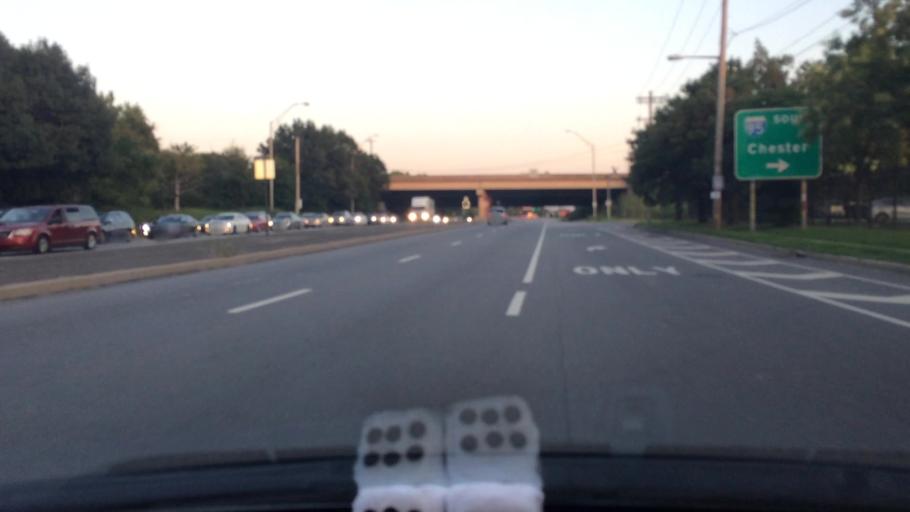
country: US
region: Pennsylvania
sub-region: Delaware County
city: Colwyn
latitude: 39.8940
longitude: -75.2365
